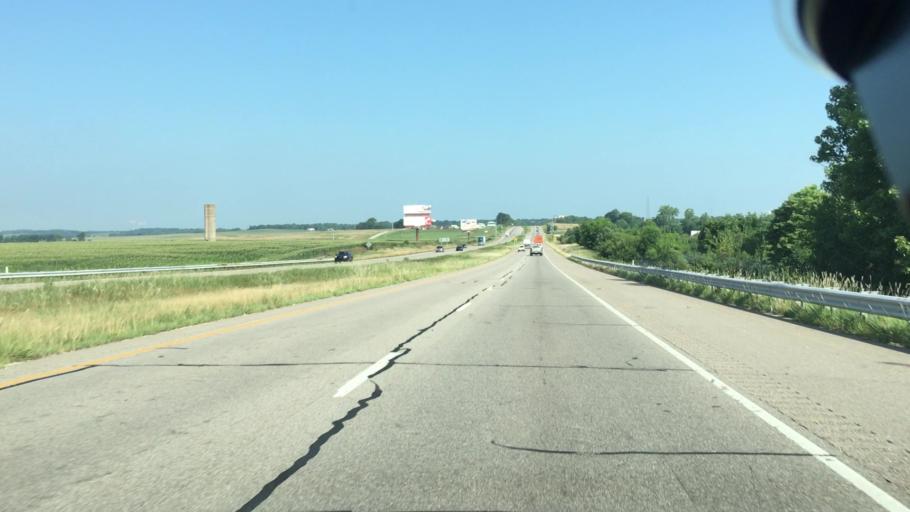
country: US
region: Indiana
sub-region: Gibson County
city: Princeton
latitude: 38.3214
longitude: -87.5772
